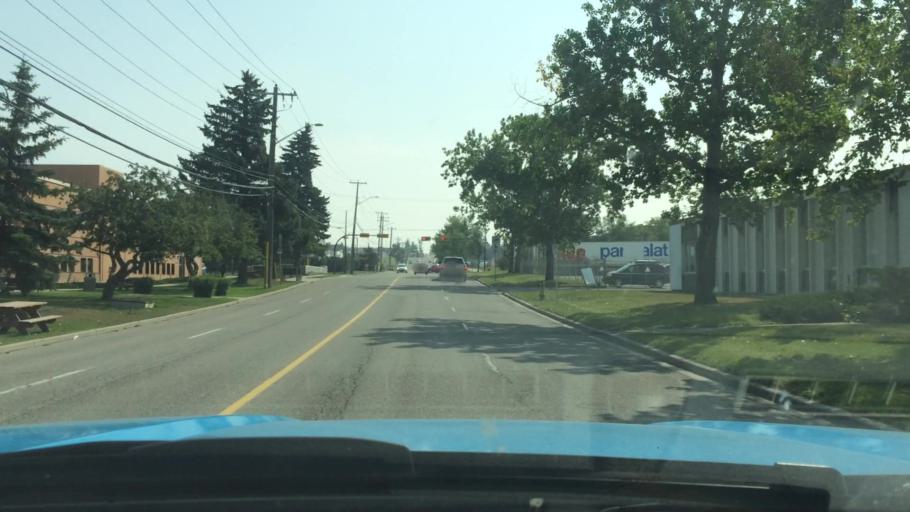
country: CA
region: Alberta
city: Calgary
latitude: 51.0524
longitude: -114.0103
